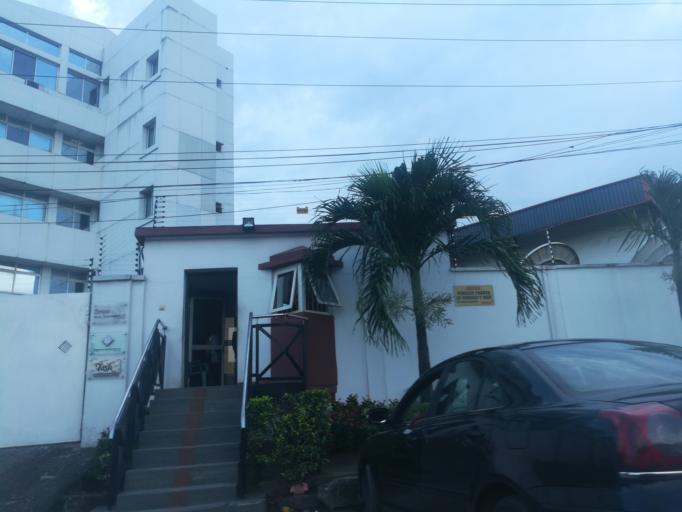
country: NG
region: Lagos
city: Somolu
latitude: 6.5524
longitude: 3.3787
